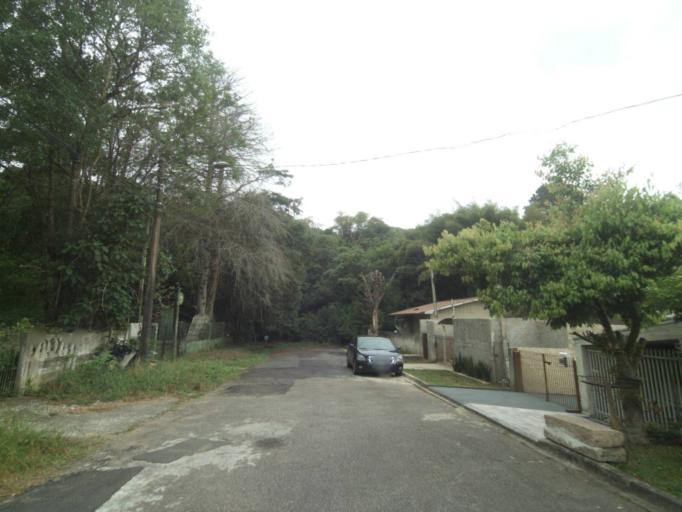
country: BR
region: Parana
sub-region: Curitiba
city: Curitiba
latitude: -25.3955
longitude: -49.3001
